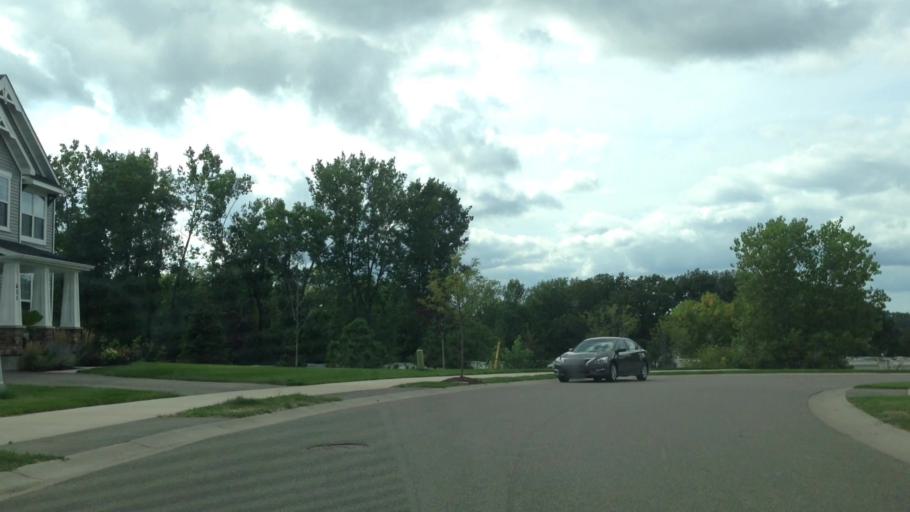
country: US
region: Minnesota
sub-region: Ramsey County
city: New Brighton
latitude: 45.0713
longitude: -93.1954
